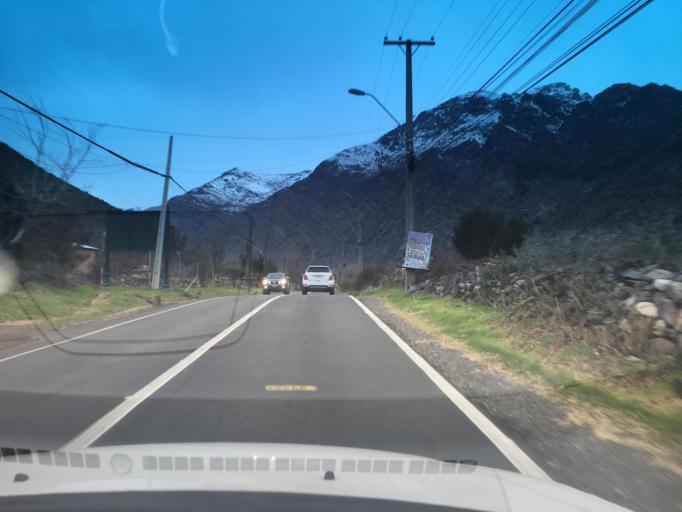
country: CL
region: Santiago Metropolitan
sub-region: Provincia de Cordillera
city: Puente Alto
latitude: -33.7092
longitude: -70.3329
